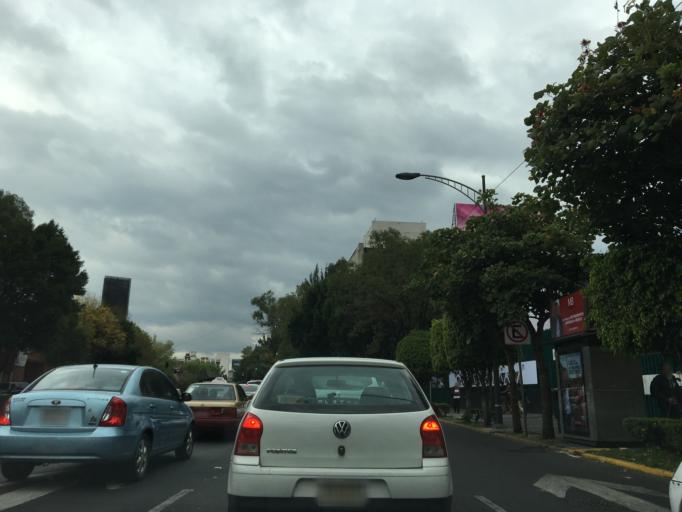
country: MX
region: Mexico City
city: Cuauhtemoc
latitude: 19.4416
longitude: -99.1548
